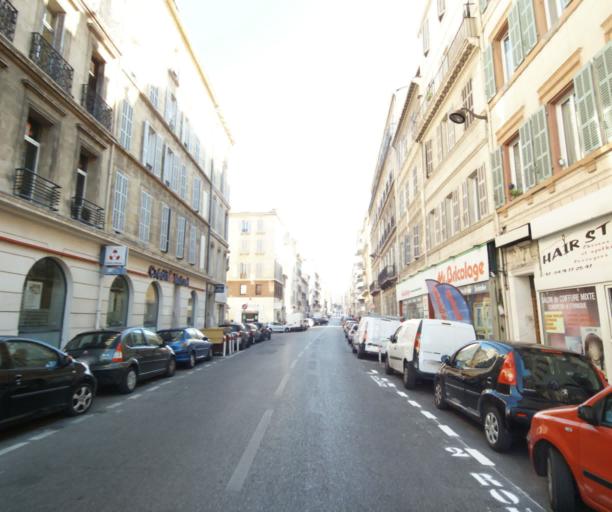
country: FR
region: Provence-Alpes-Cote d'Azur
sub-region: Departement des Bouches-du-Rhone
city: Marseille 06
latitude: 43.2860
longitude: 5.3851
